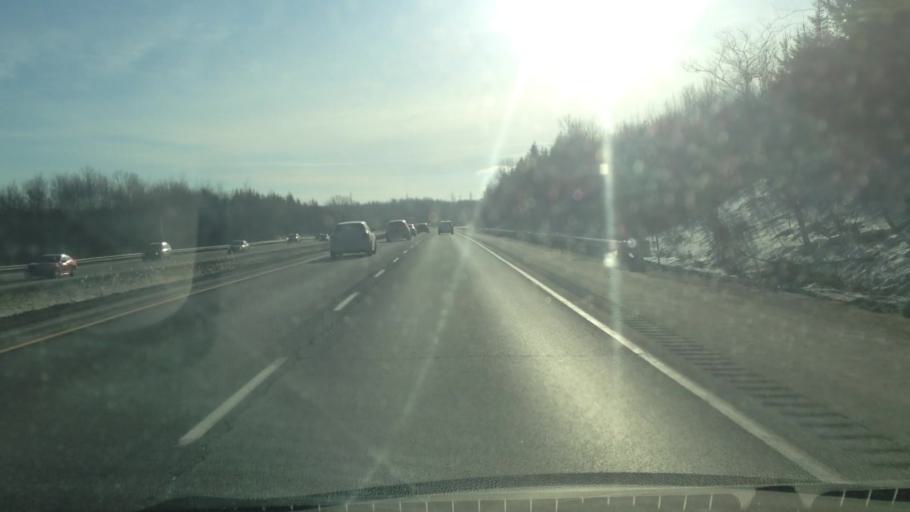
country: CA
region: Quebec
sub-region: Laurentides
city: Prevost
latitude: 45.8339
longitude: -74.0632
